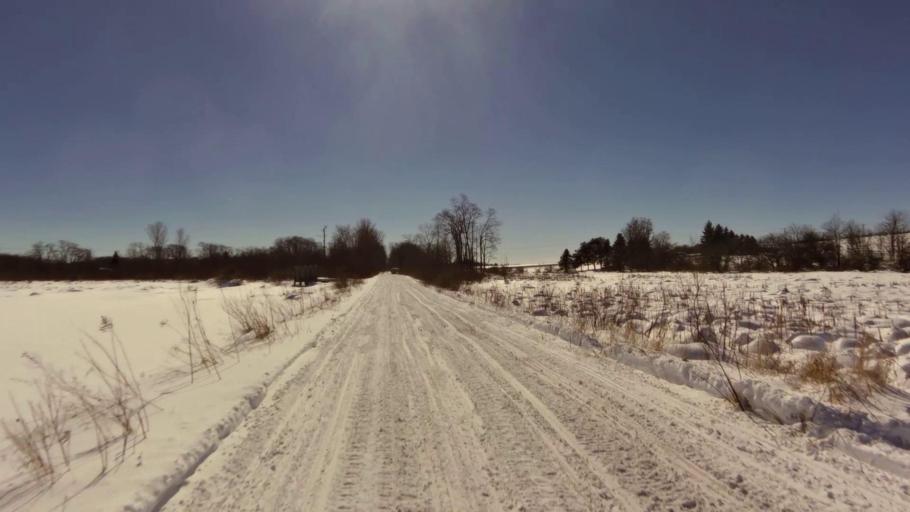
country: US
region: New York
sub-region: Chautauqua County
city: Mayville
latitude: 42.1757
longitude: -79.5819
